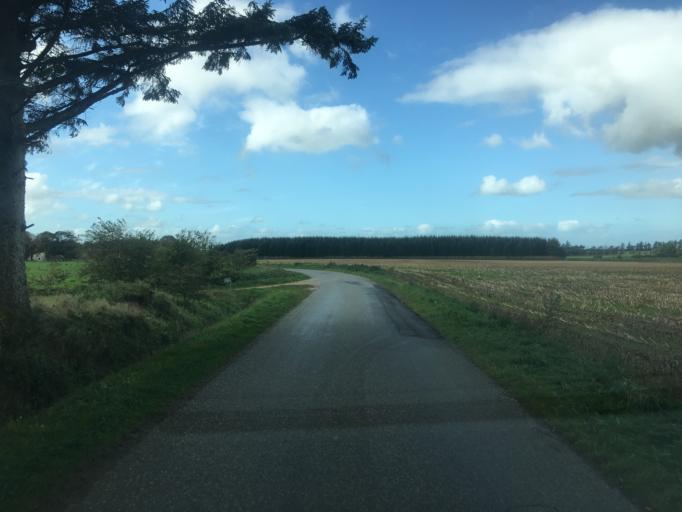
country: DK
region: South Denmark
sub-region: Tonder Kommune
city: Logumkloster
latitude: 55.1082
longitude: 8.8788
